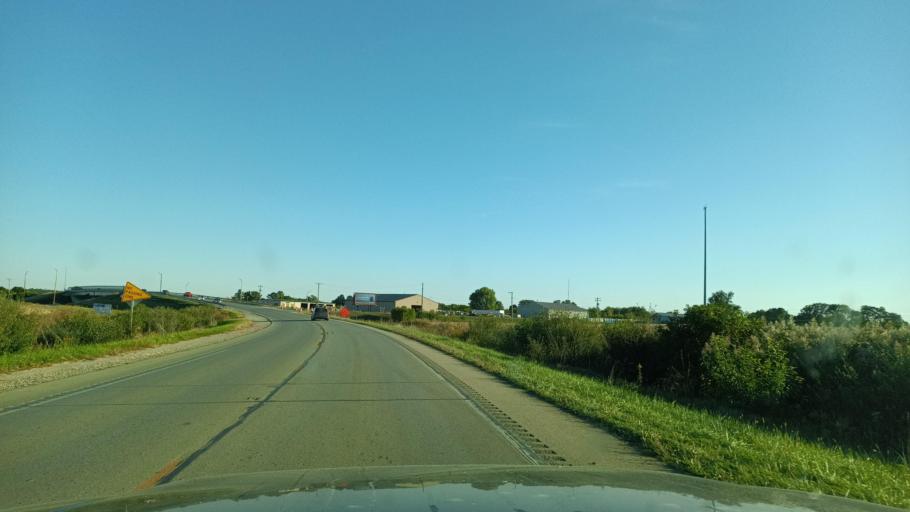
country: US
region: Illinois
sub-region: Champaign County
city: Champaign
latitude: 40.1449
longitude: -88.2895
